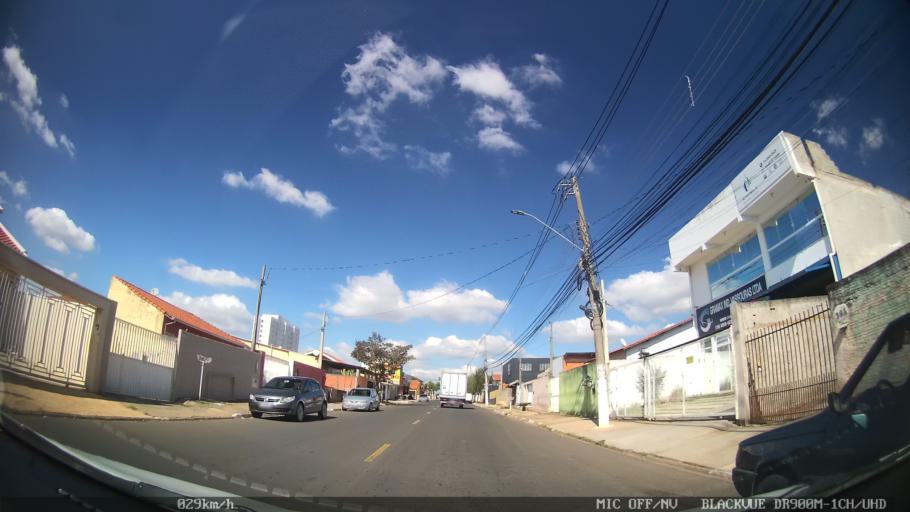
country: BR
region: Sao Paulo
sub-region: Hortolandia
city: Hortolandia
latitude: -22.8877
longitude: -47.2225
